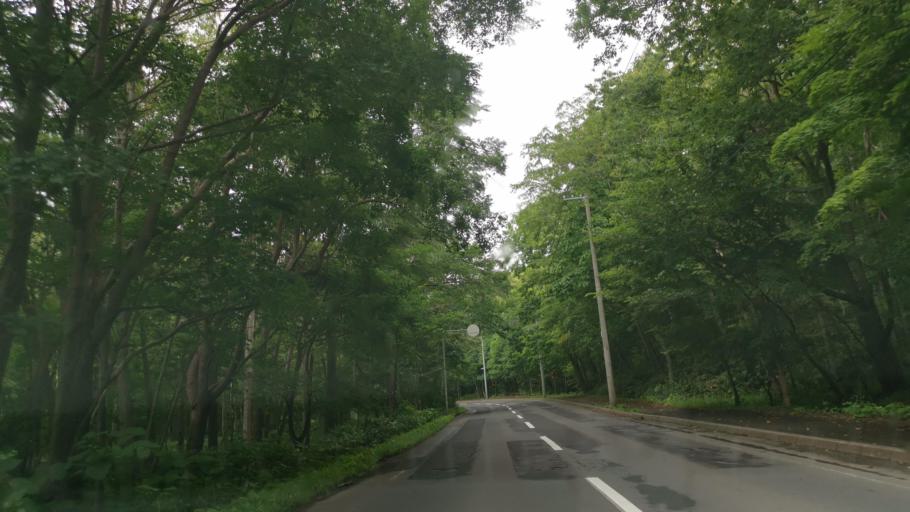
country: JP
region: Hokkaido
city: Sapporo
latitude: 42.9790
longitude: 141.3599
